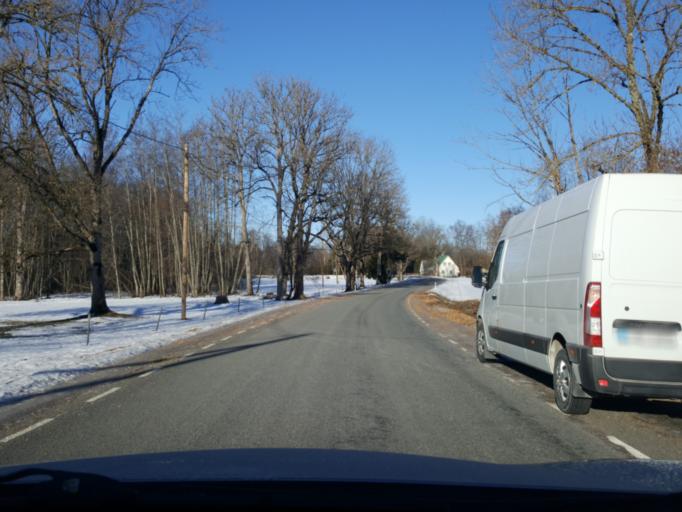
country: EE
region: Viljandimaa
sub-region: Viljandi linn
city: Viljandi
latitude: 58.4176
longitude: 25.5438
